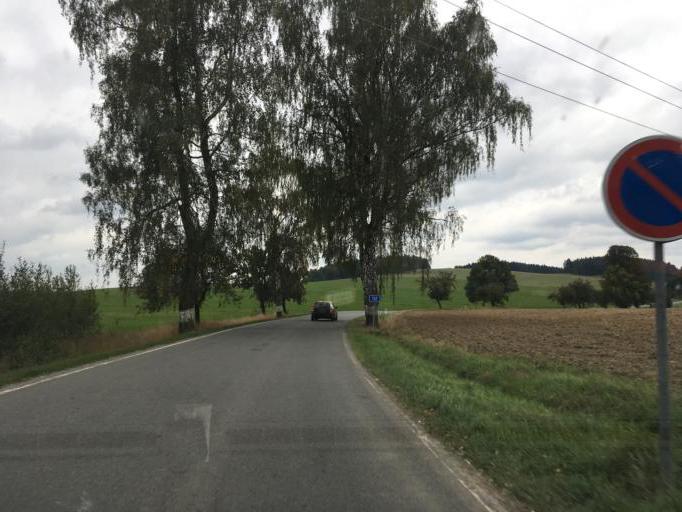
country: CZ
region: Vysocina
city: Horni Cerekev
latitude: 49.3150
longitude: 15.3343
